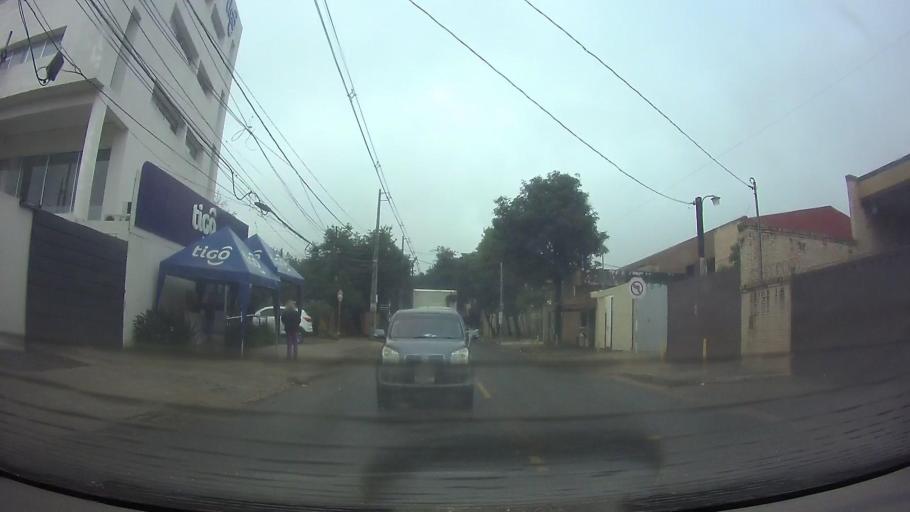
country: PY
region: Central
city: Villa Elisa
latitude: -25.3474
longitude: -57.5721
